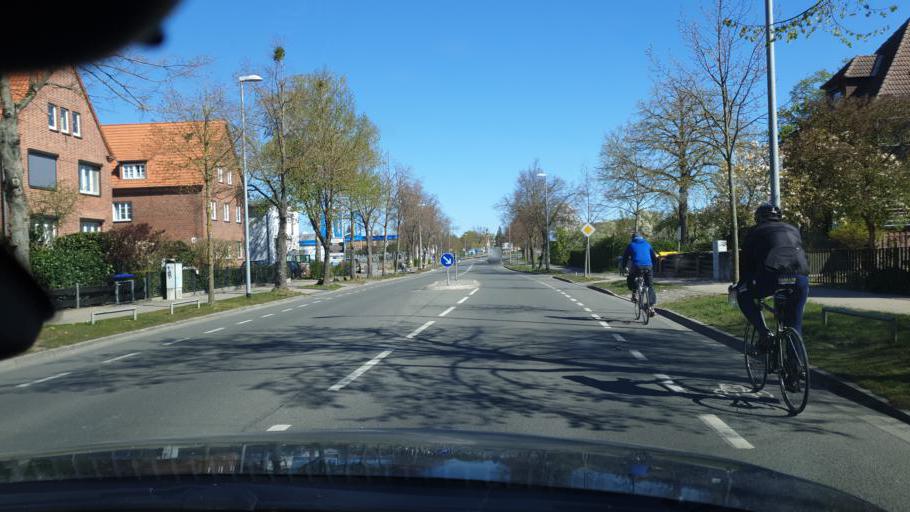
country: DE
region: Mecklenburg-Vorpommern
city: Werdervorstadt
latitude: 53.6420
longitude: 11.4248
